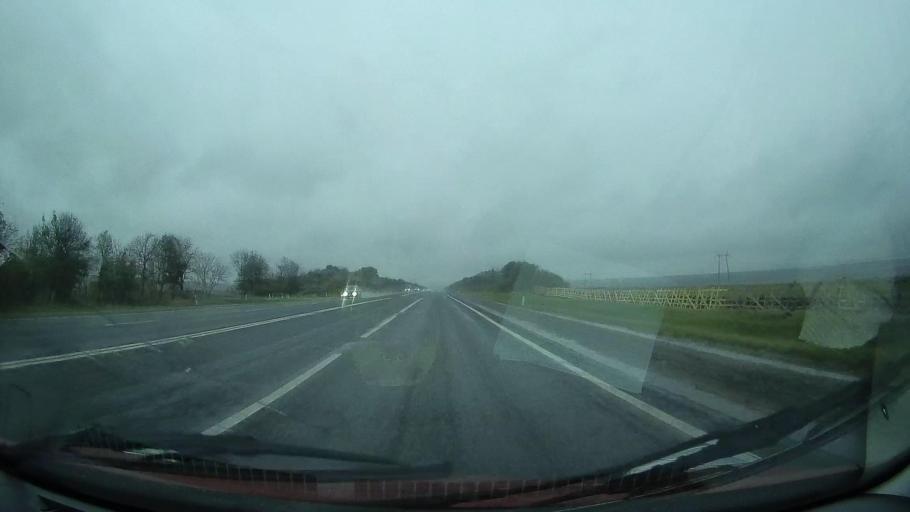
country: RU
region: Stavropol'skiy
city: Nevinnomyssk
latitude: 44.6150
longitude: 42.1089
